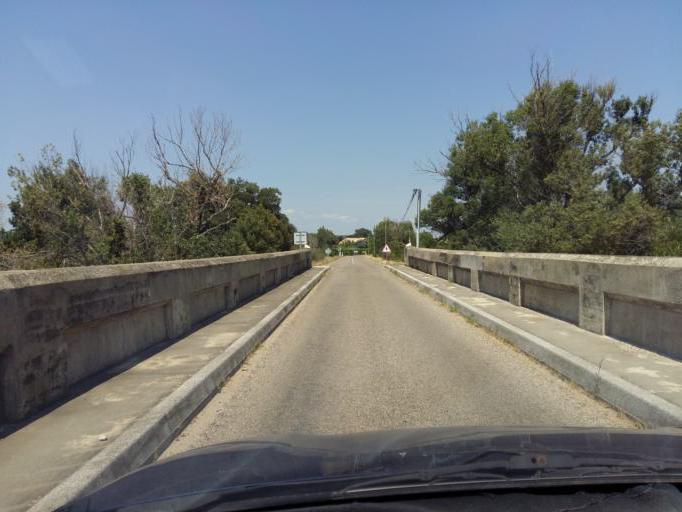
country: FR
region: Provence-Alpes-Cote d'Azur
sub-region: Departement du Vaucluse
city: Camaret-sur-Aigues
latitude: 44.1893
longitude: 4.8906
